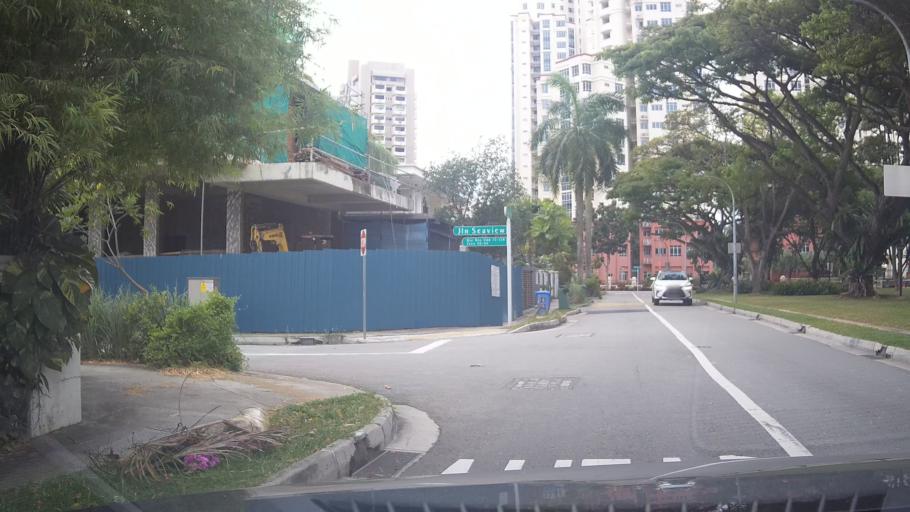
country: SG
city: Singapore
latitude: 1.2992
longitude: 103.8945
